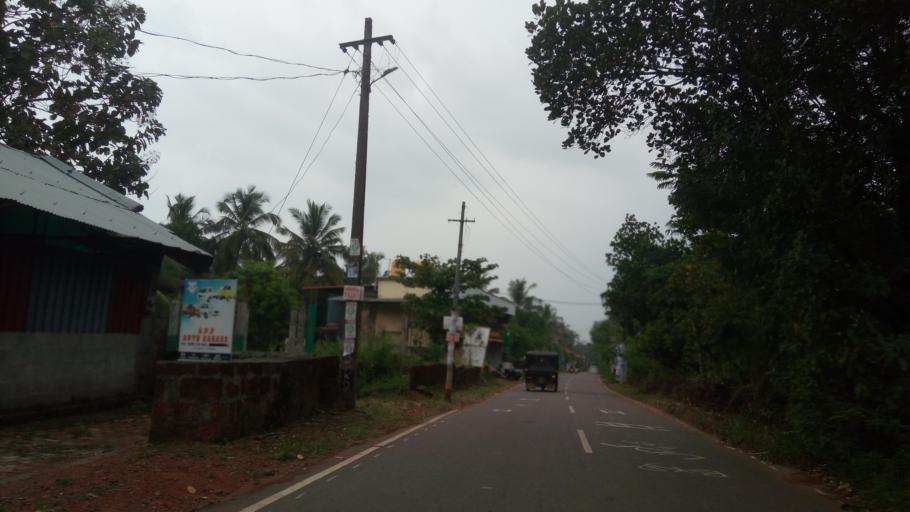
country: IN
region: Kerala
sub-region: Malappuram
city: Malappuram
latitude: 10.9761
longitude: 76.0076
